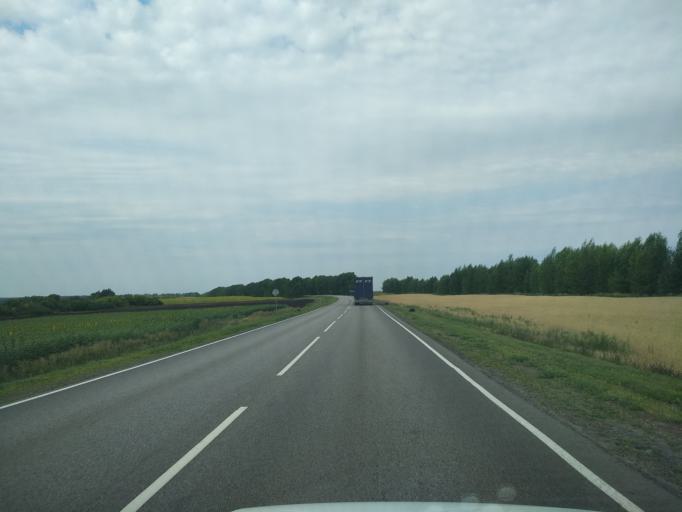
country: RU
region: Voronezj
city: Pereleshinskiy
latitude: 51.8507
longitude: 40.3210
